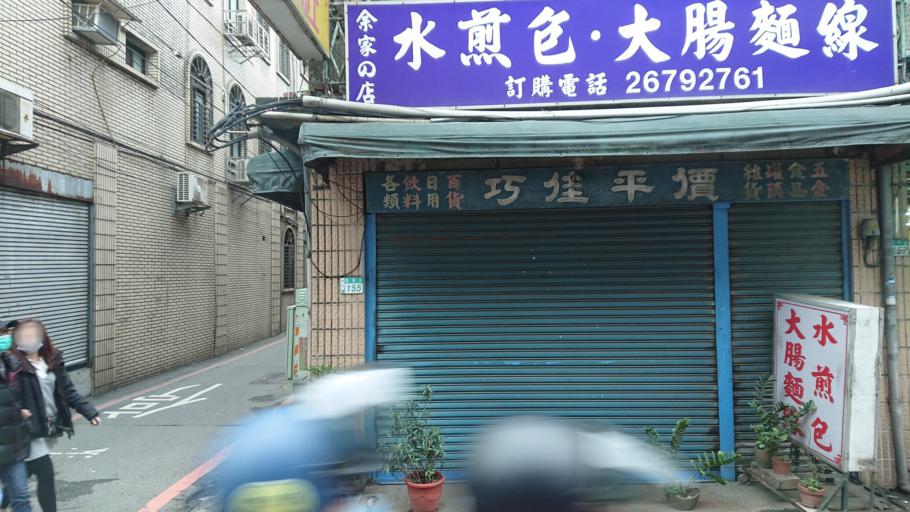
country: TW
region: Taiwan
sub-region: Taoyuan
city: Taoyuan
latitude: 24.9533
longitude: 121.3511
